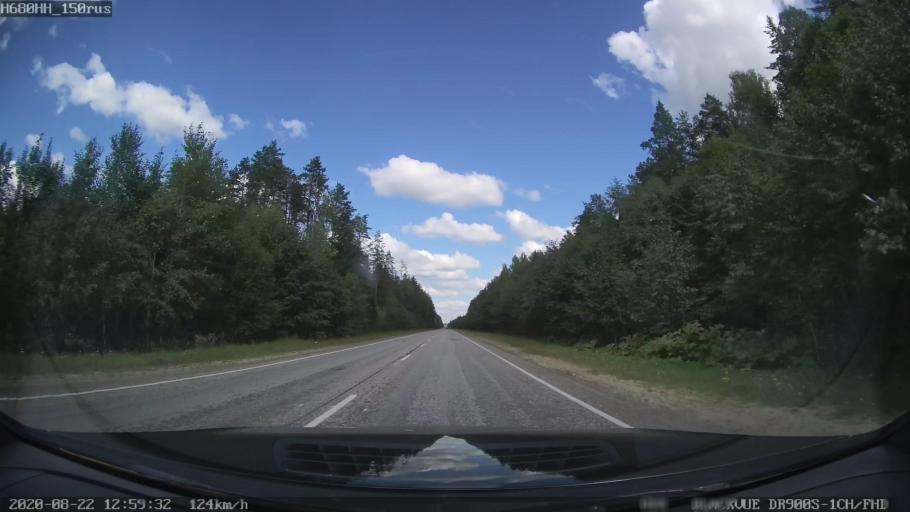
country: RU
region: Tverskaya
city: Bezhetsk
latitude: 57.6077
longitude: 36.3613
